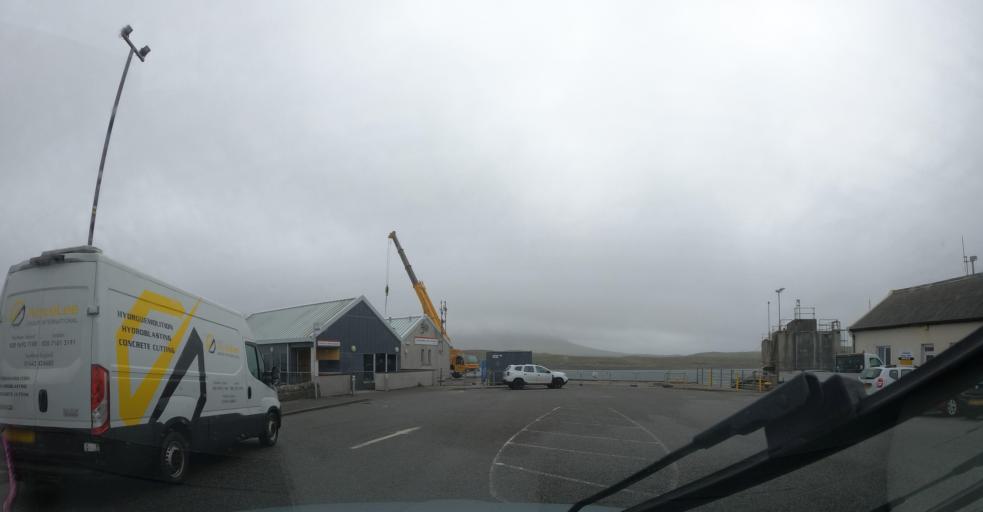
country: GB
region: Scotland
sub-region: Eilean Siar
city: Isle of North Uist
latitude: 57.5969
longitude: -7.1570
